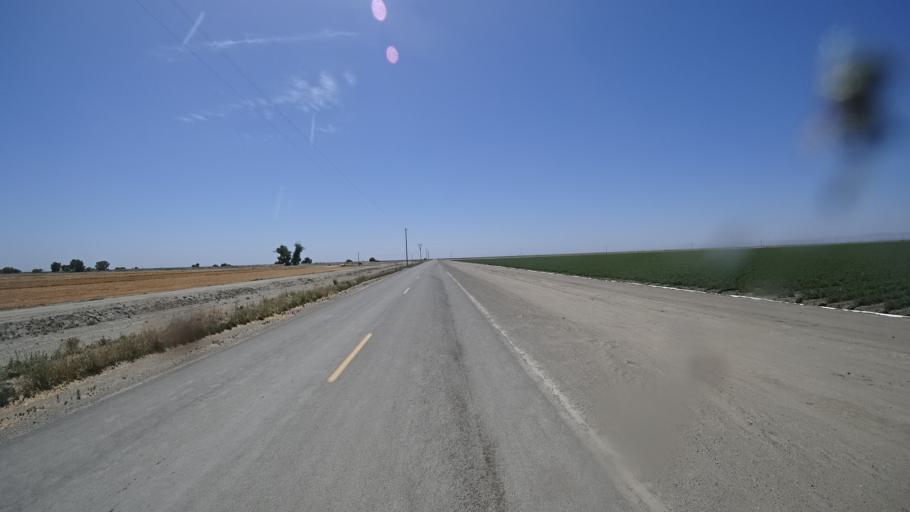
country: US
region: California
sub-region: Kings County
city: Stratford
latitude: 36.1473
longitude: -119.7444
